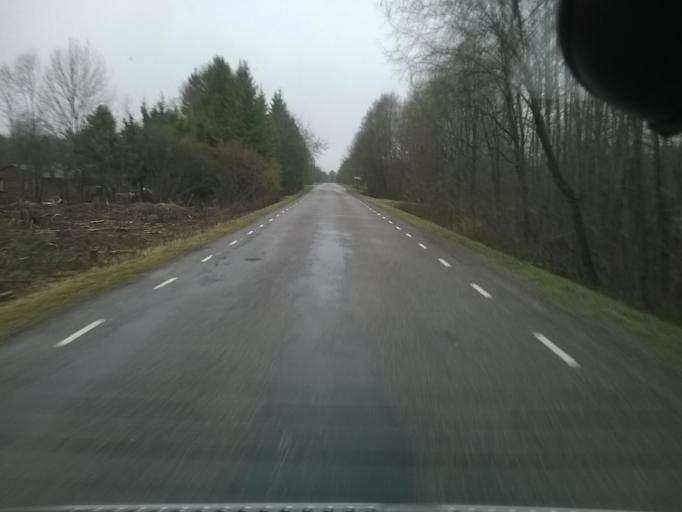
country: EE
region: Raplamaa
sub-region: Kohila vald
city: Kohila
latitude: 59.2041
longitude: 24.6673
